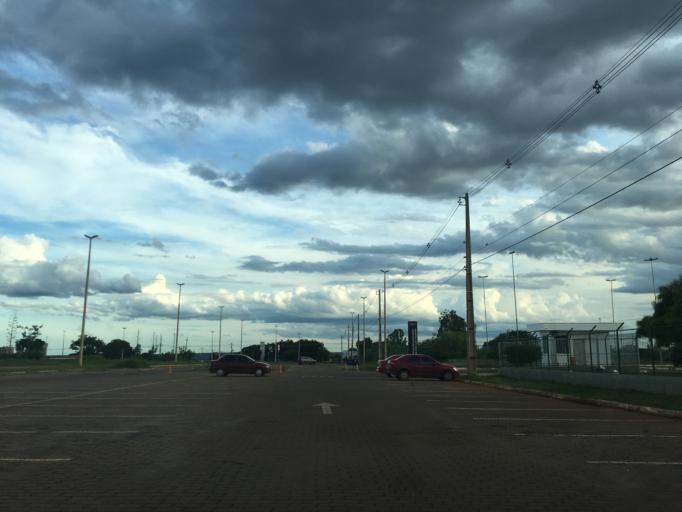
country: BR
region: Federal District
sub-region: Brasilia
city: Brasilia
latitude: -15.8310
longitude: -47.9433
